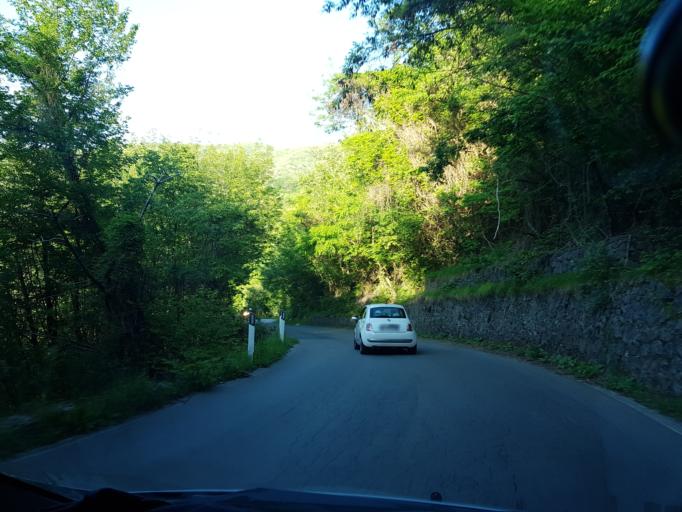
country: IT
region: Tuscany
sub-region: Provincia di Lucca
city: Minucciano
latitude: 44.1785
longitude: 10.1996
